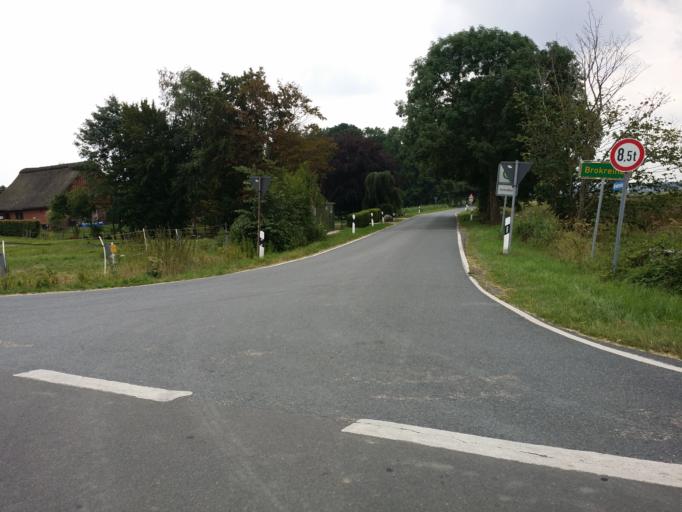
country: DE
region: Schleswig-Holstein
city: Krempermoor
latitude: 53.8758
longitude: 9.4601
